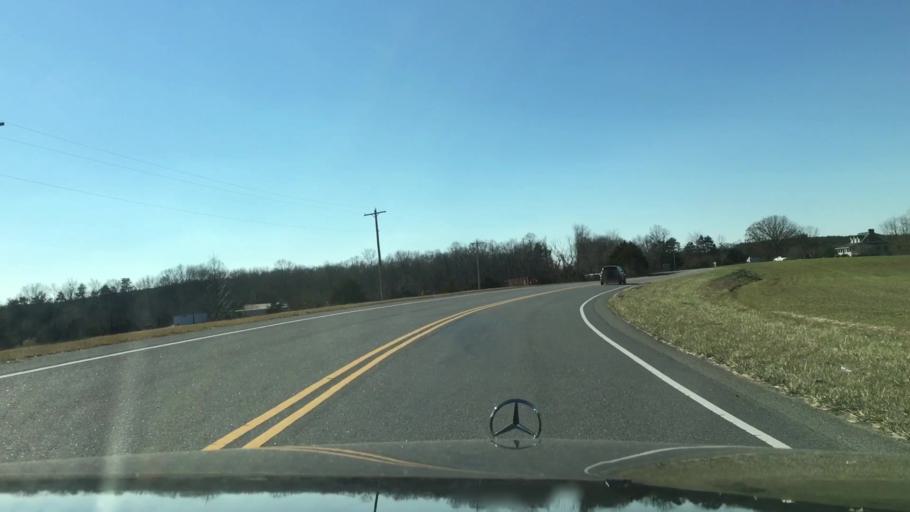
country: US
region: Virginia
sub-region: City of Bedford
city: Bedford
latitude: 37.2127
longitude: -79.4371
